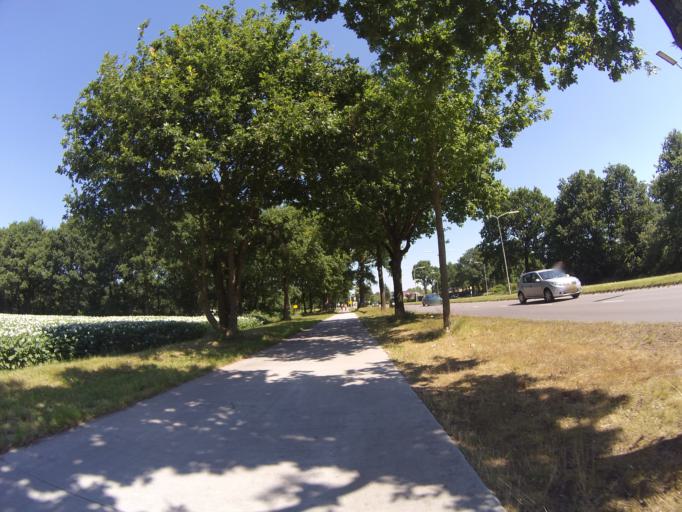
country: NL
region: Drenthe
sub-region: Gemeente Emmen
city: Emmen
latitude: 52.7613
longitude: 6.8744
